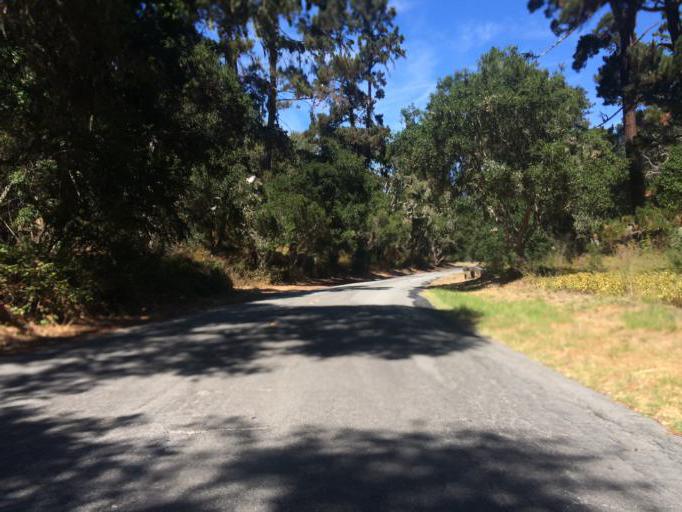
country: US
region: California
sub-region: Monterey County
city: Monterey
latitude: 36.5885
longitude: -121.8899
